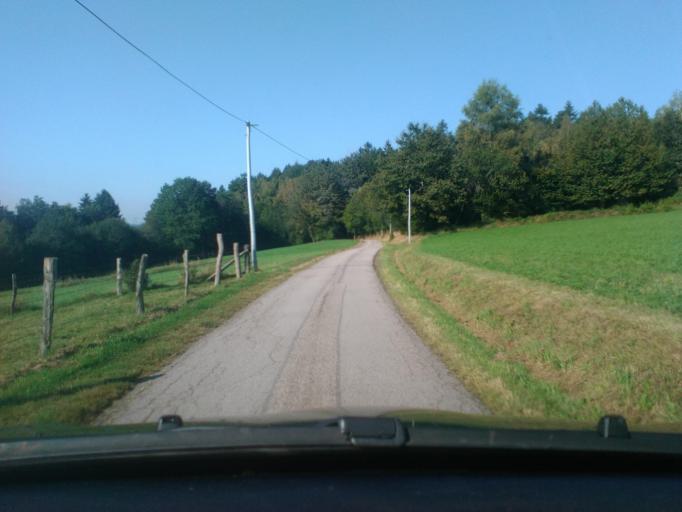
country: FR
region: Lorraine
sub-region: Departement des Vosges
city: Moyenmoutier
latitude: 48.3630
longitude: 6.9063
